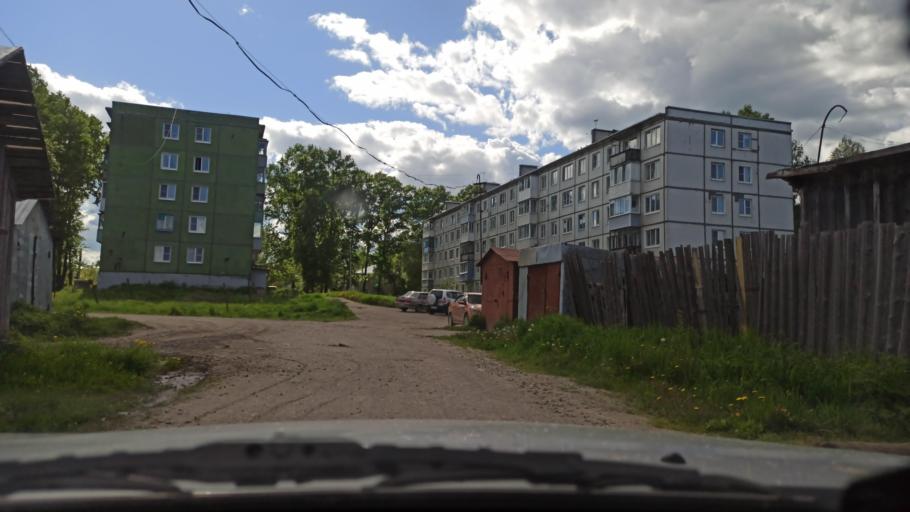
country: RU
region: Vologda
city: Vologda
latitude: 59.3428
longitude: 39.8160
